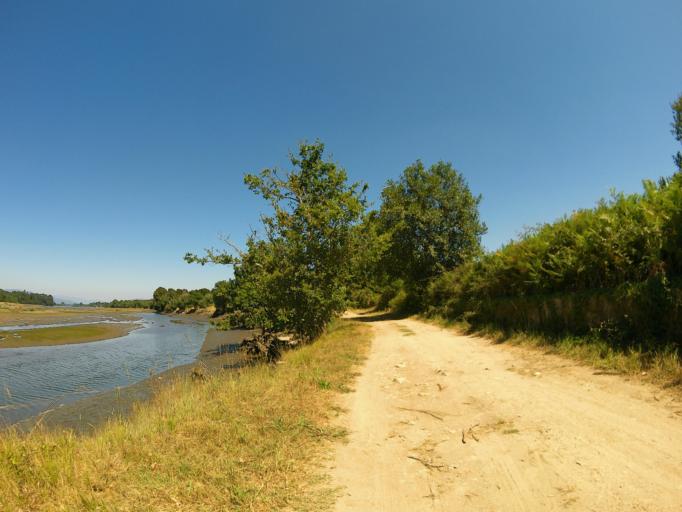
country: PT
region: Viana do Castelo
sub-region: Viana do Castelo
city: Darque
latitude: 41.7000
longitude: -8.7366
